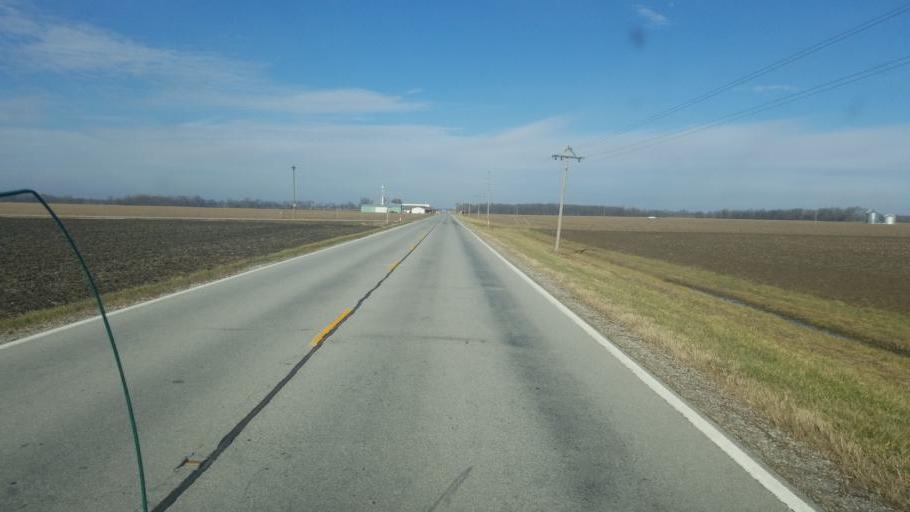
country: US
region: Illinois
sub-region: Saline County
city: Eldorado
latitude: 37.8658
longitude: -88.4529
